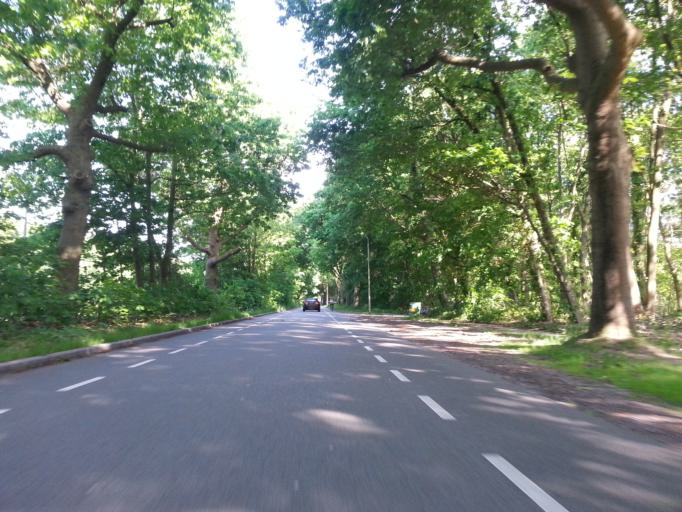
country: NL
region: Utrecht
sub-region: Gemeente Amersfoort
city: Amersfoort
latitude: 52.1351
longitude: 5.3659
